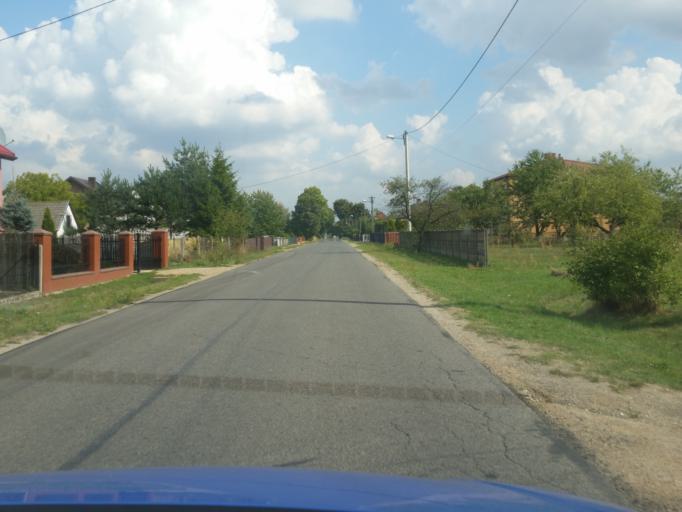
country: PL
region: Silesian Voivodeship
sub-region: Powiat czestochowski
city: Klomnice
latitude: 50.9652
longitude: 19.3218
